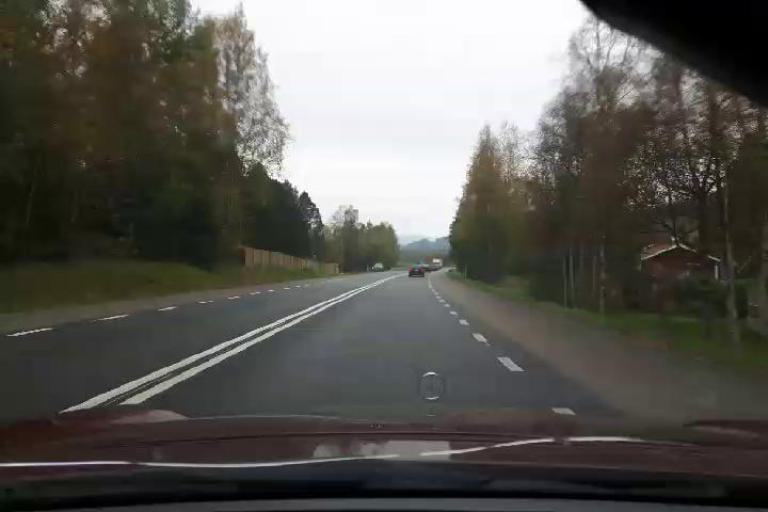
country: SE
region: Vaesternorrland
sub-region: OErnskoeldsviks Kommun
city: Ornskoldsvik
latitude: 63.2962
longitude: 18.6665
